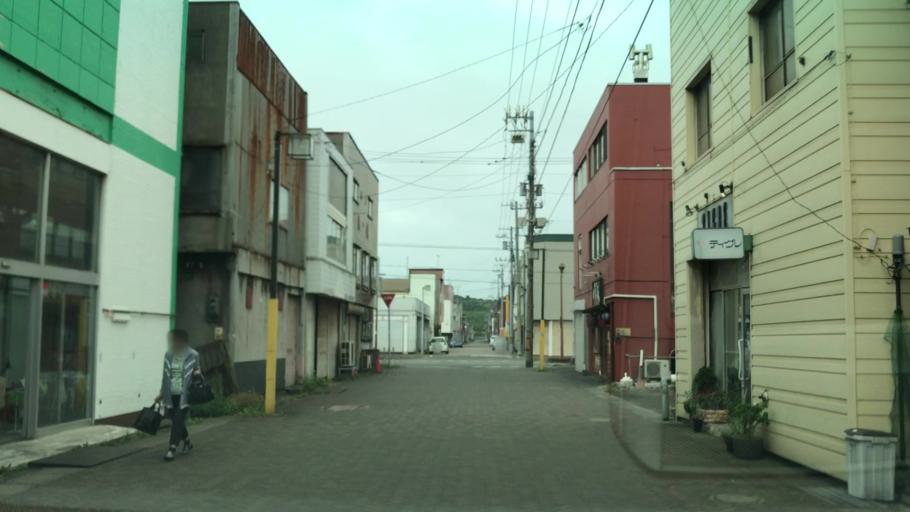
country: JP
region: Hokkaido
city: Muroran
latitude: 42.3344
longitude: 141.0105
